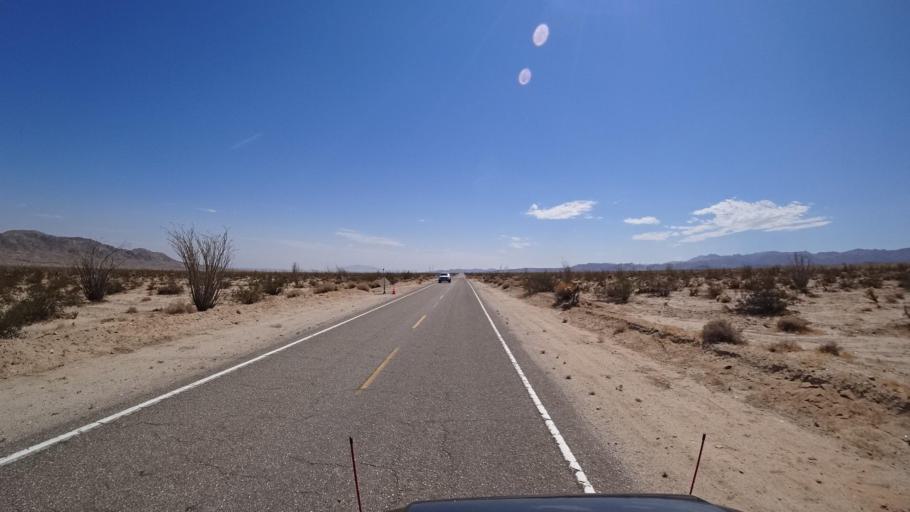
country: MX
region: Baja California
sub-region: Tecate
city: Cereso del Hongo
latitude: 32.7865
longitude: -116.0992
